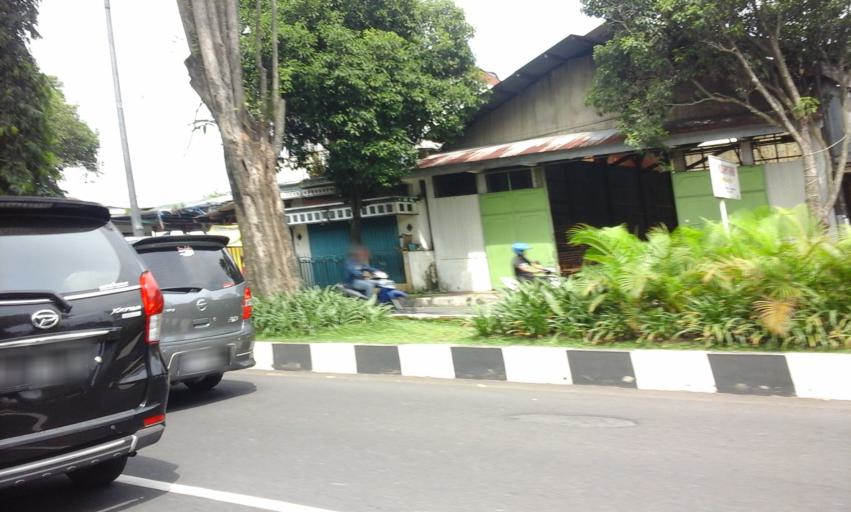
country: ID
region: East Java
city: Kaliwates
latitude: -8.1821
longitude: 113.6727
